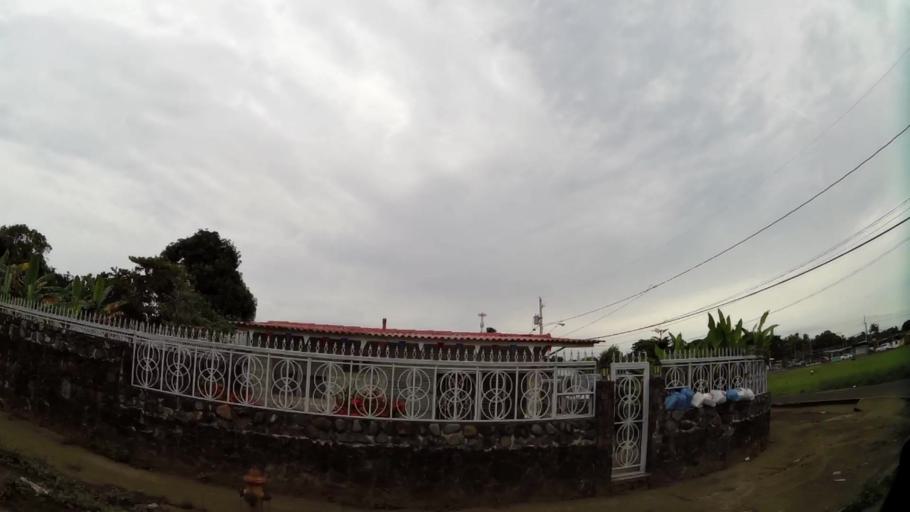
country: PA
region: Panama
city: San Miguelito
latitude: 9.0408
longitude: -79.4433
